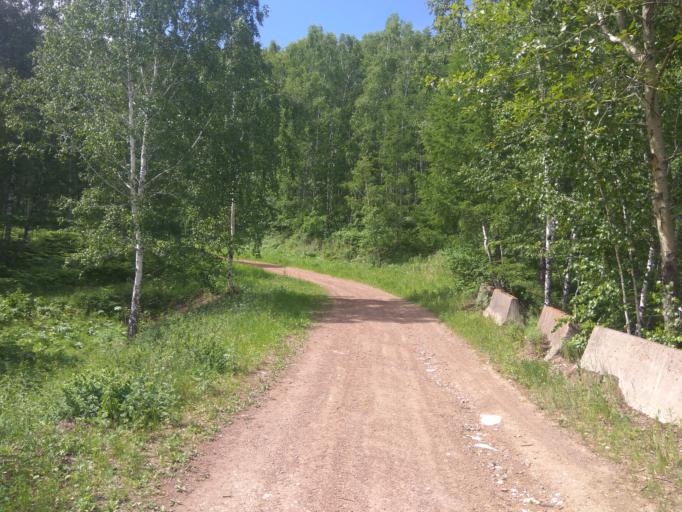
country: RU
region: Krasnoyarskiy
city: Krasnoyarsk
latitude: 55.9617
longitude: 92.8584
